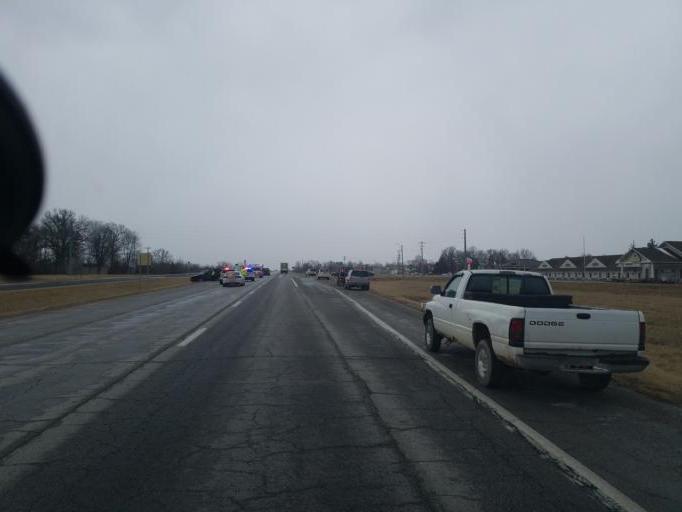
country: US
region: Missouri
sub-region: Macon County
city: La Plata
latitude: 40.0358
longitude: -92.4897
